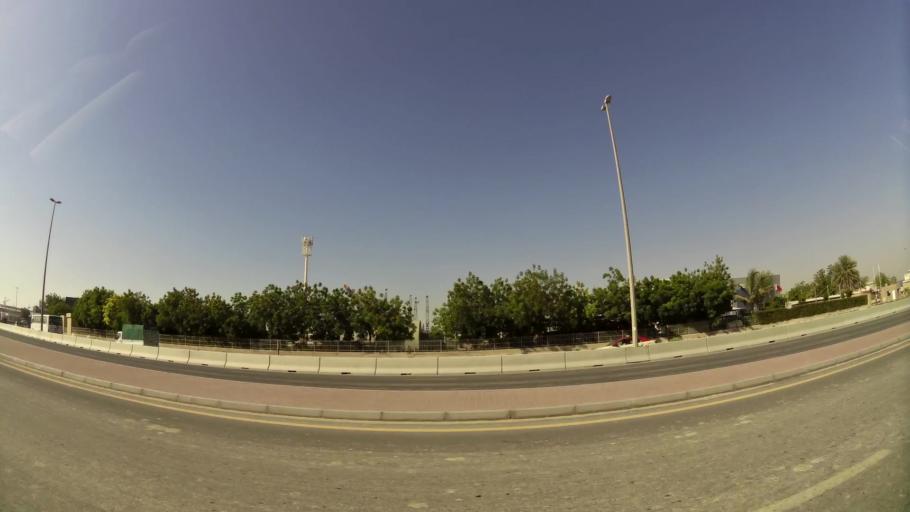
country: AE
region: Dubai
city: Dubai
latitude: 24.9917
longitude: 55.1072
